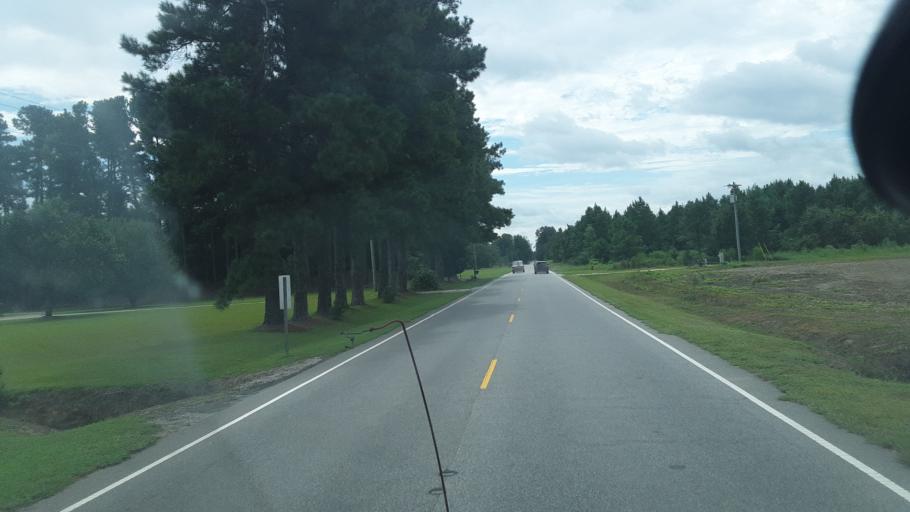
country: US
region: North Carolina
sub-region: Robeson County
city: Rowland
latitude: 34.6202
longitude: -79.3341
